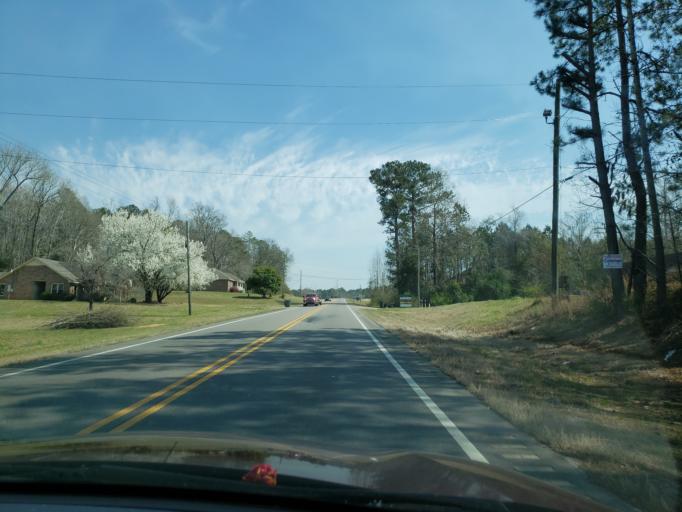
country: US
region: Alabama
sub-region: Elmore County
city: Wetumpka
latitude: 32.5522
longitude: -86.1819
